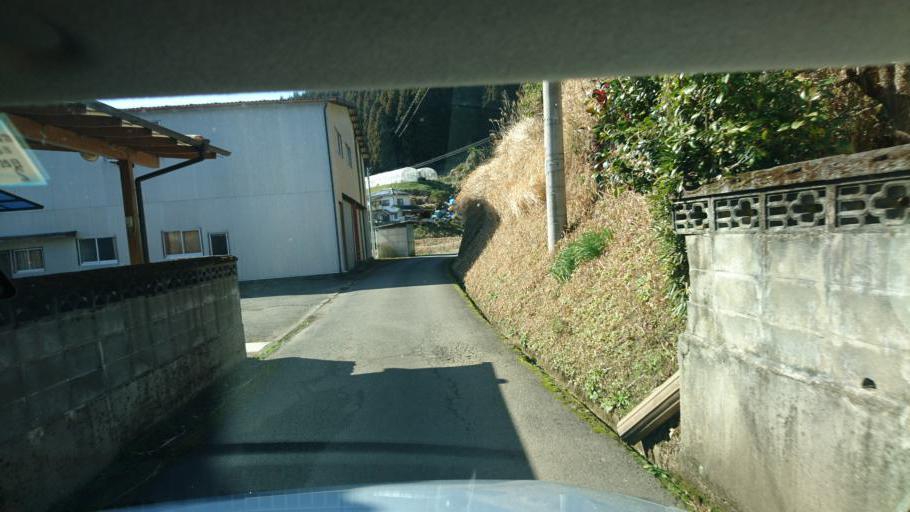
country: JP
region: Oita
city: Takedamachi
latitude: 32.7216
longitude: 131.3037
